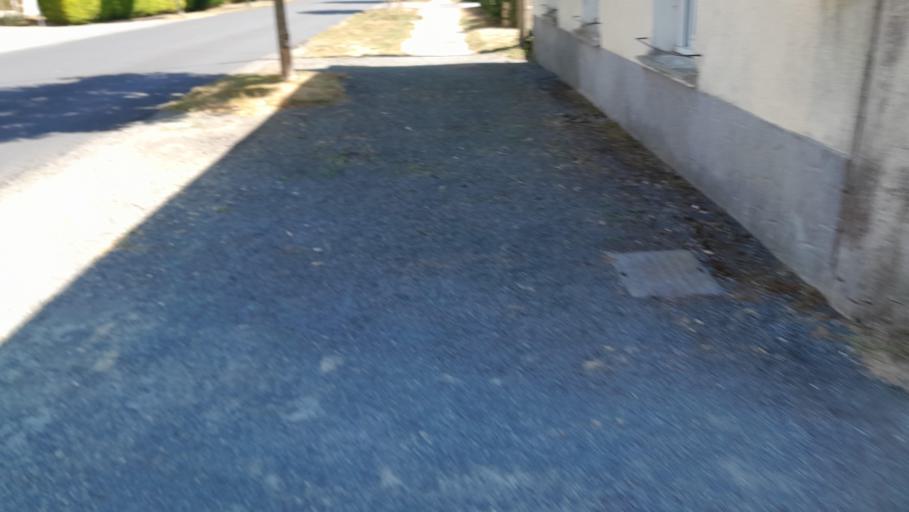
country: FR
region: Brittany
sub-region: Departement d'Ille-et-Vilaine
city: Le Pertre
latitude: 47.9662
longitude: -1.0546
